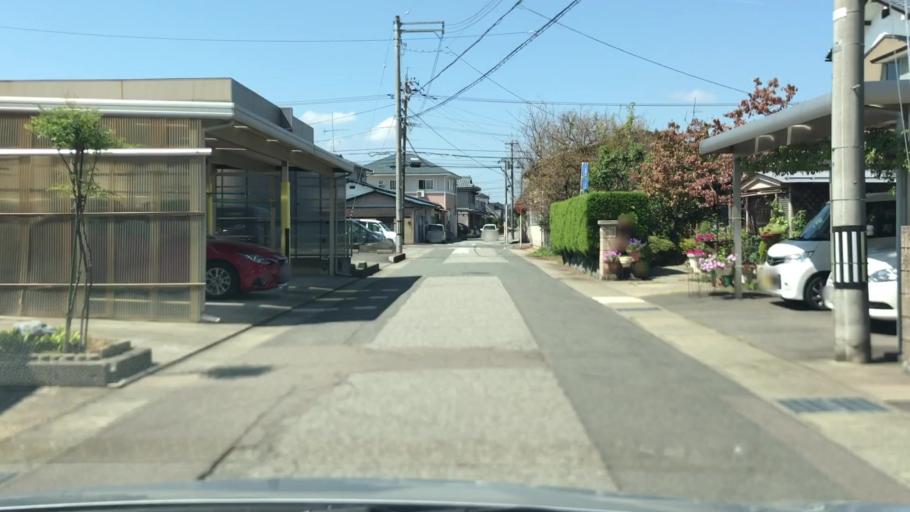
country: JP
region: Fukui
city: Maruoka
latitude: 36.1259
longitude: 136.2183
